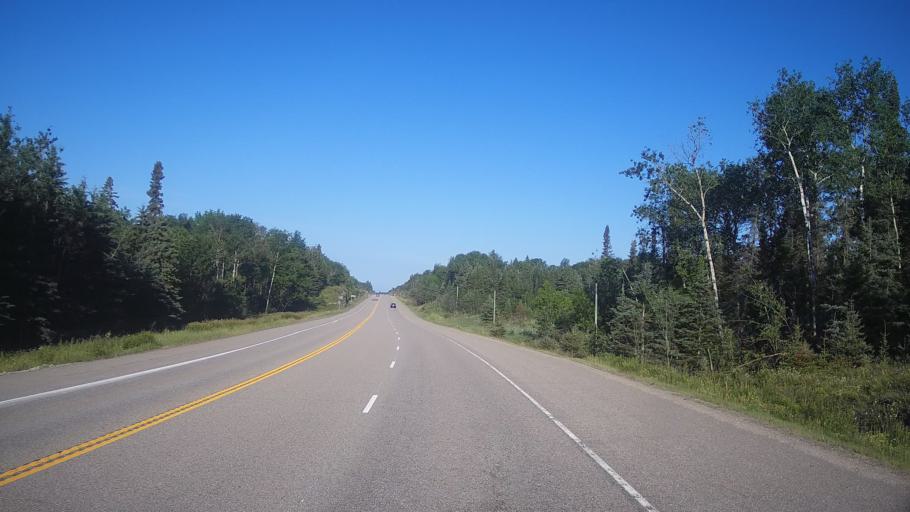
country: US
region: Minnesota
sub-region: Roseau County
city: Warroad
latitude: 49.7189
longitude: -94.7305
